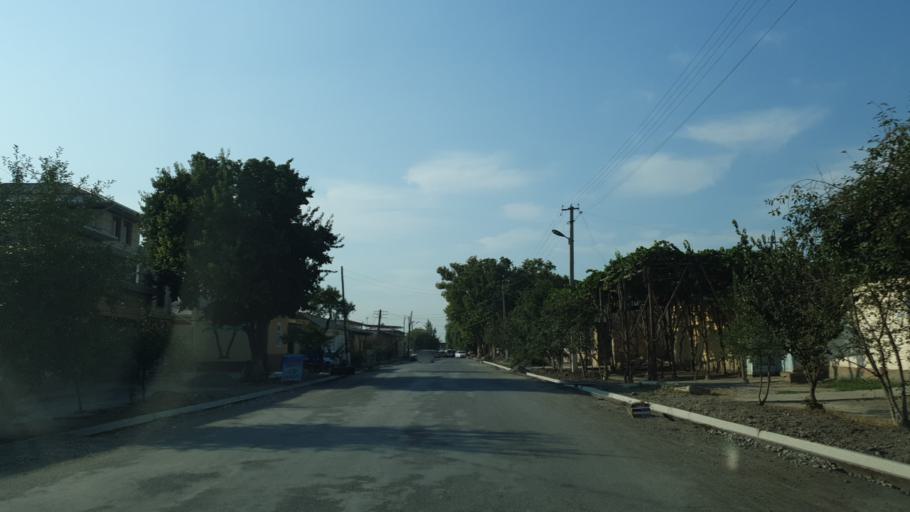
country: UZ
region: Fergana
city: Yaypan
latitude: 40.3772
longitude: 70.8116
